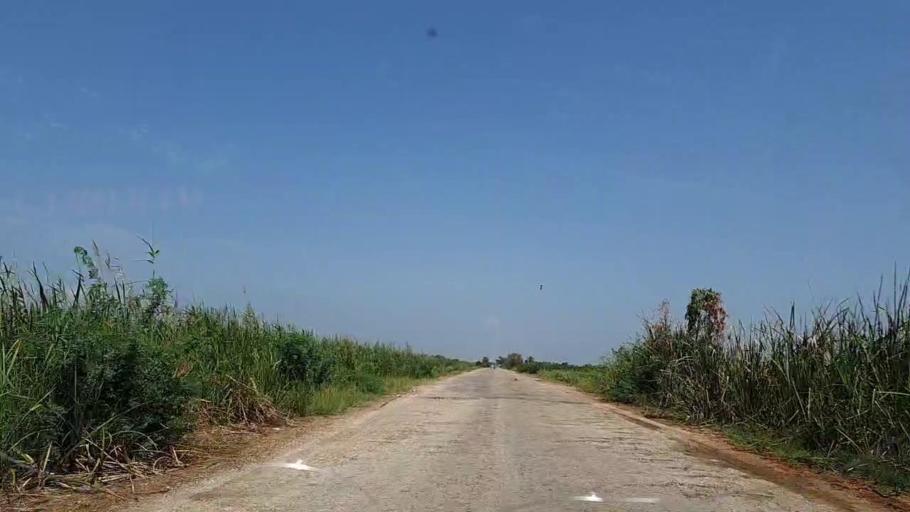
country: PK
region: Sindh
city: Naushahro Firoz
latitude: 26.8173
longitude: 68.1780
